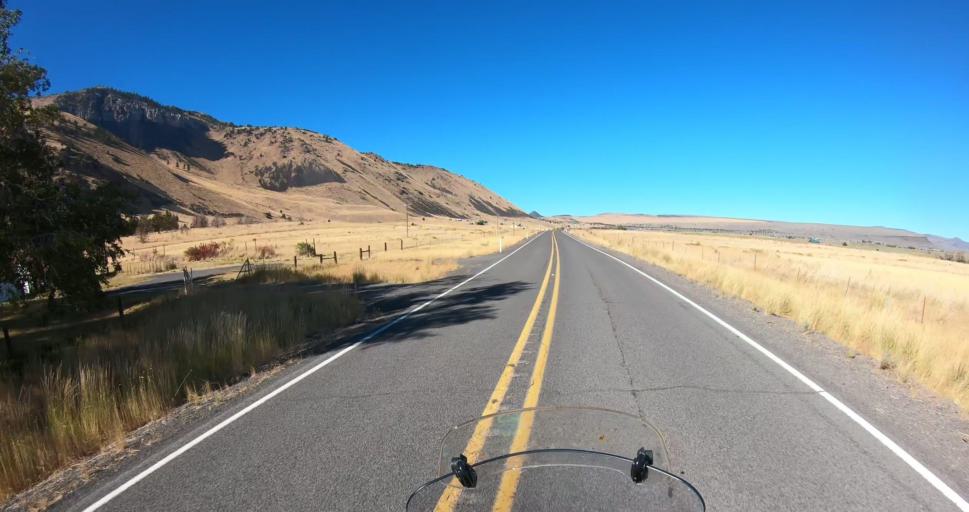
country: US
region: Oregon
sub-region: Lake County
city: Lakeview
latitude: 42.9743
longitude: -120.7777
